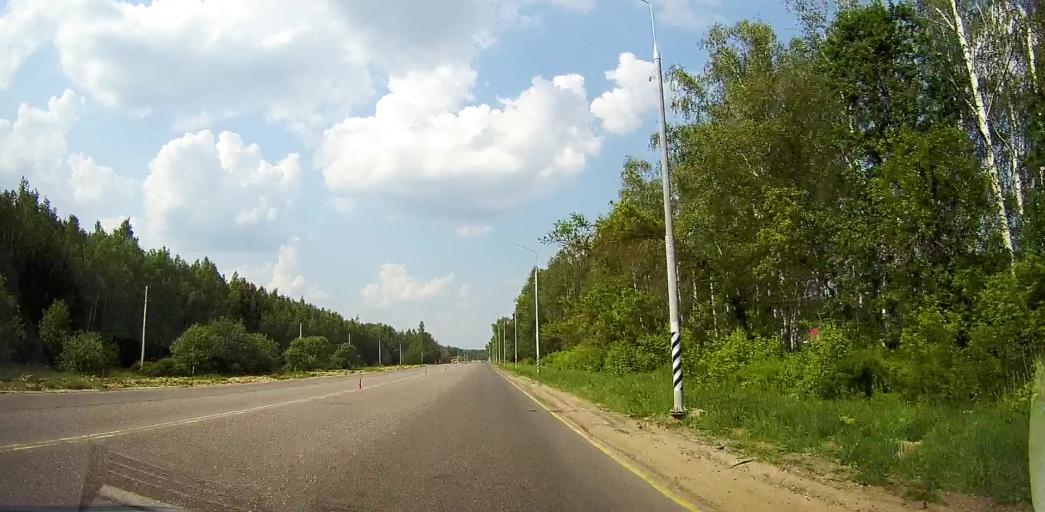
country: RU
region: Moskovskaya
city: Mikhnevo
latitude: 55.0656
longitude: 37.9534
